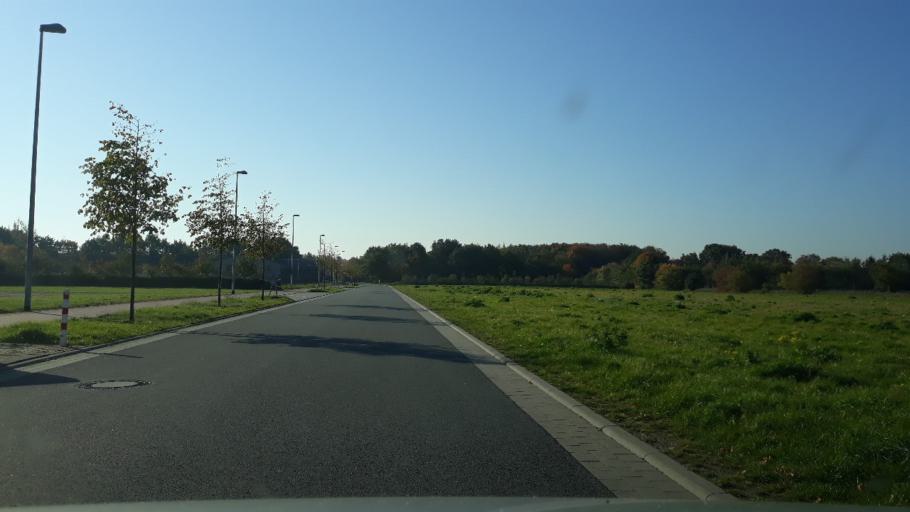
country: DE
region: Schleswig-Holstein
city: Kropp
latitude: 54.4179
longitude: 9.5220
